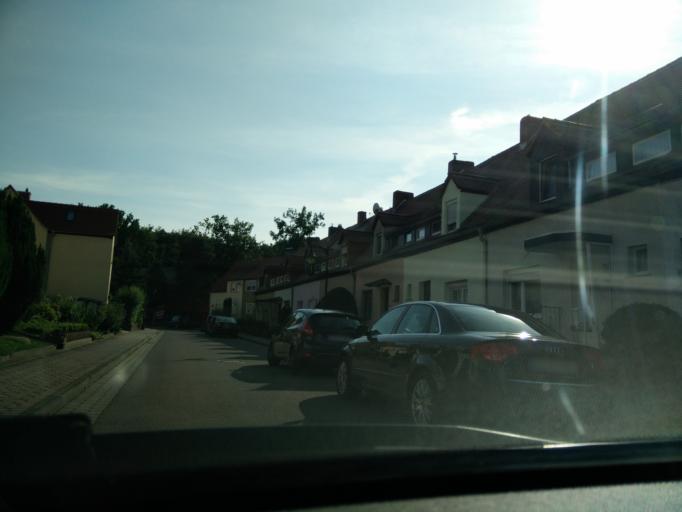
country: DE
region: Saxony
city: Kitzscher
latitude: 51.1641
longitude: 12.5491
